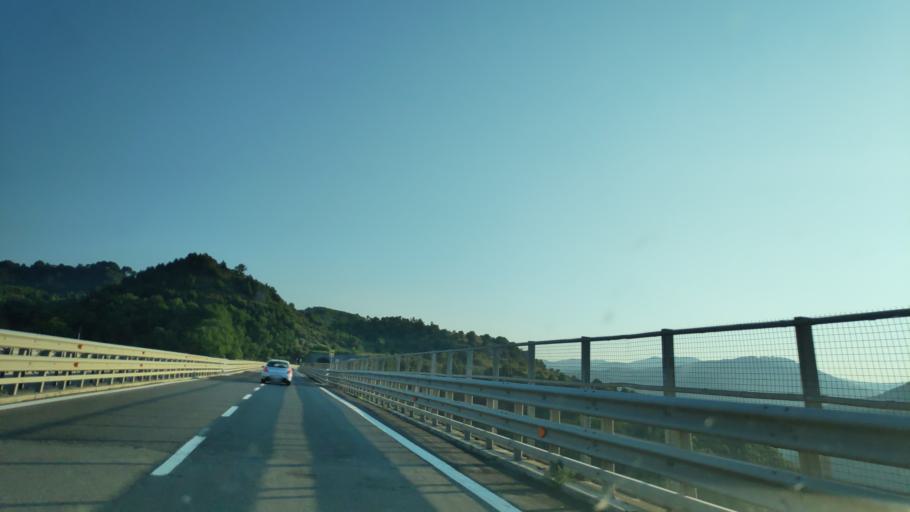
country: IT
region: Calabria
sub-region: Provincia di Cosenza
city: Carpanzano
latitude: 39.1493
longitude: 16.2827
